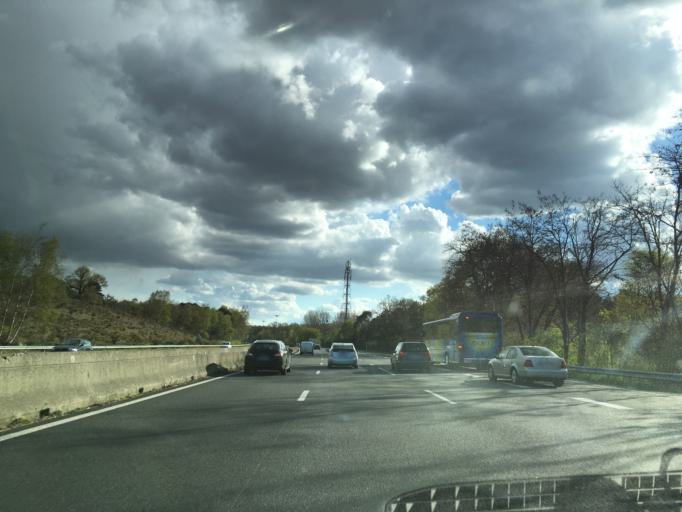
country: FR
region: Picardie
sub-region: Departement de l'Oise
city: Thiers-sur-Theve
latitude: 49.1317
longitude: 2.5603
